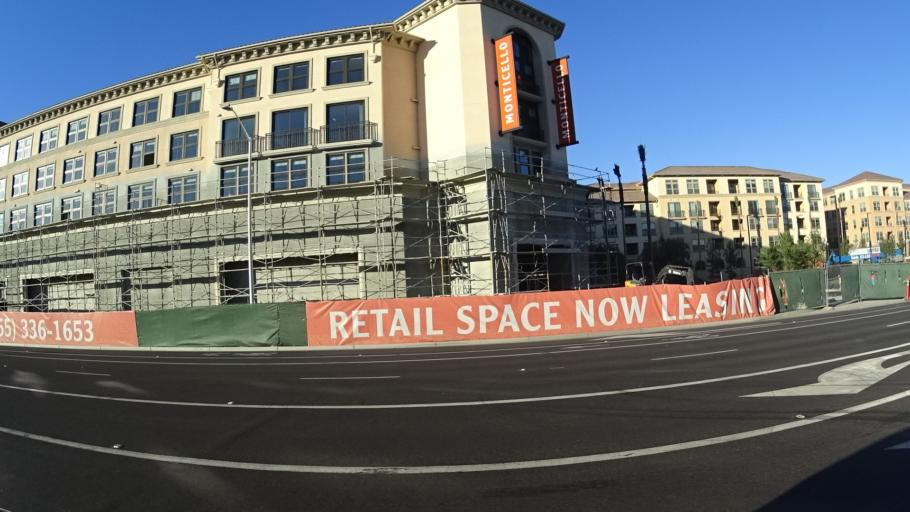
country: US
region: California
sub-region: Santa Clara County
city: Sunnyvale
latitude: 37.3668
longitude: -121.9951
